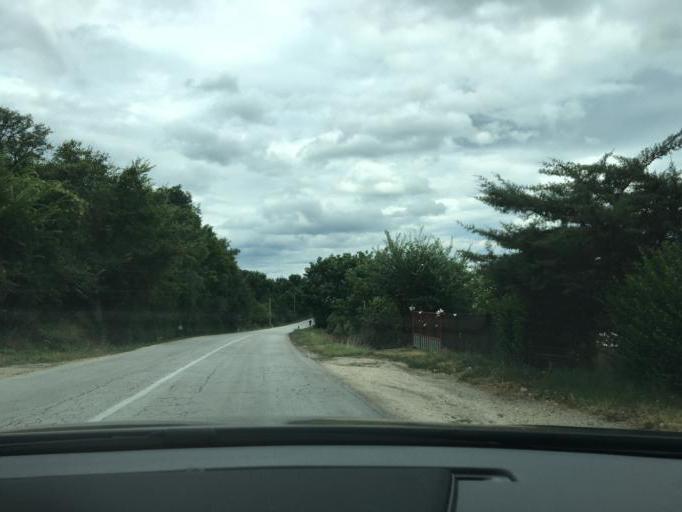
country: MK
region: Kriva Palanka
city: Kriva Palanka
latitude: 42.1767
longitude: 22.2570
